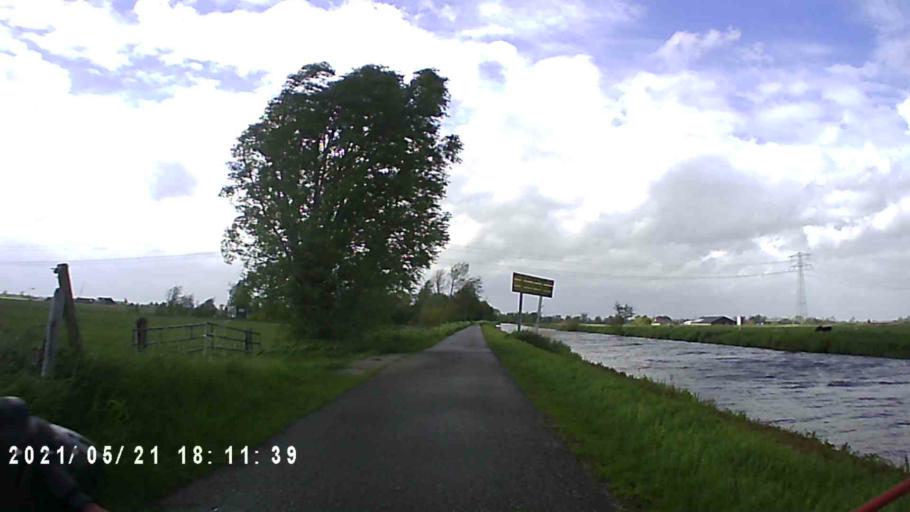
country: NL
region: Groningen
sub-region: Gemeente Zuidhorn
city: Zuidhorn
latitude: 53.2076
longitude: 6.4118
